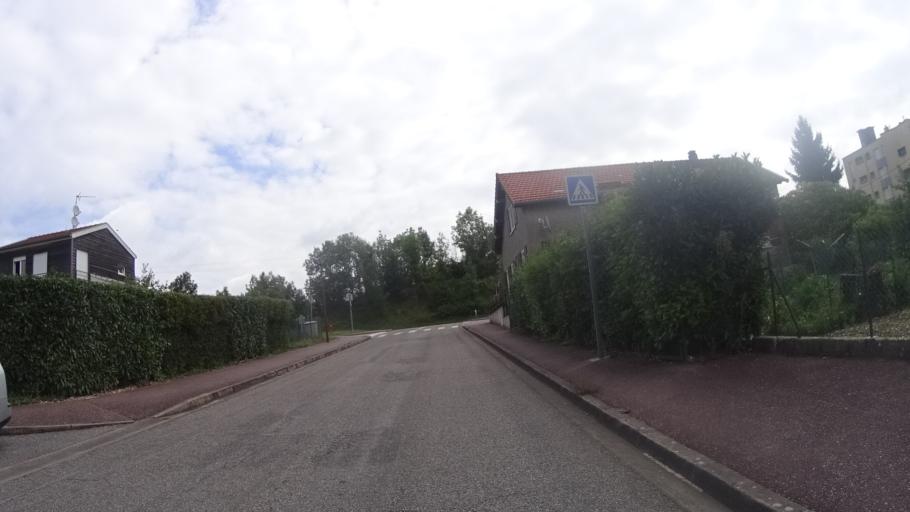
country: FR
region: Lorraine
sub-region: Departement de la Meuse
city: Tronville-en-Barrois
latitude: 48.7221
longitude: 5.2839
